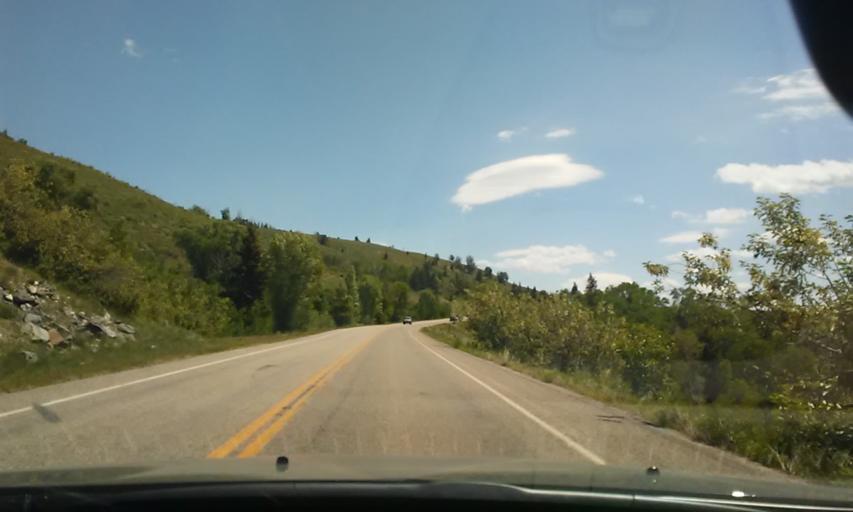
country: US
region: Wyoming
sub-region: Teton County
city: Jackson
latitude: 43.8387
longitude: -110.4923
